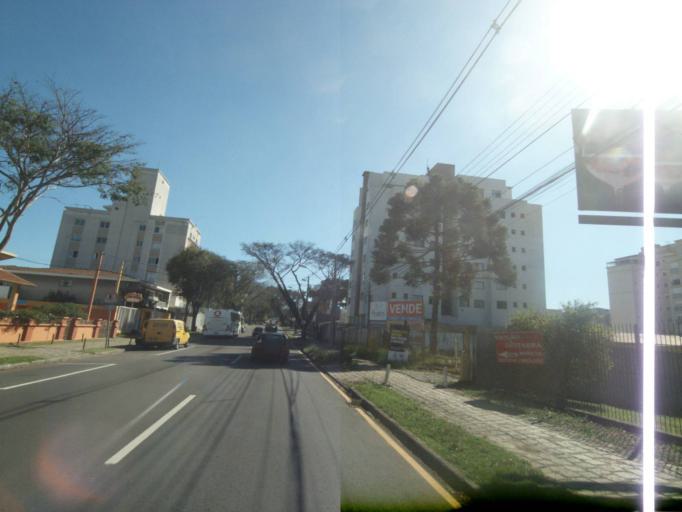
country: BR
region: Parana
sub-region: Curitiba
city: Curitiba
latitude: -25.3986
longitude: -49.2379
